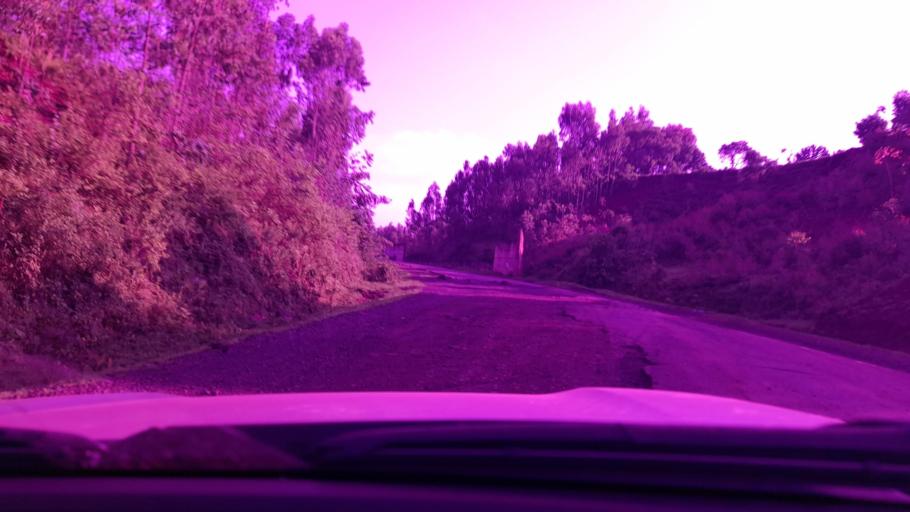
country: ET
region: Oromiya
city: Bedele
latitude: 8.1481
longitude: 36.4602
